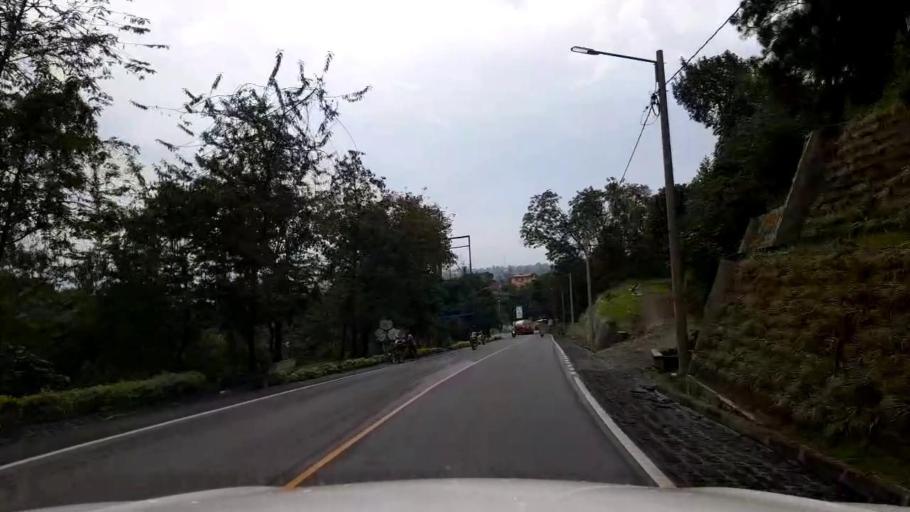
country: RW
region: Western Province
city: Gisenyi
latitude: -1.7039
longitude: 29.2647
